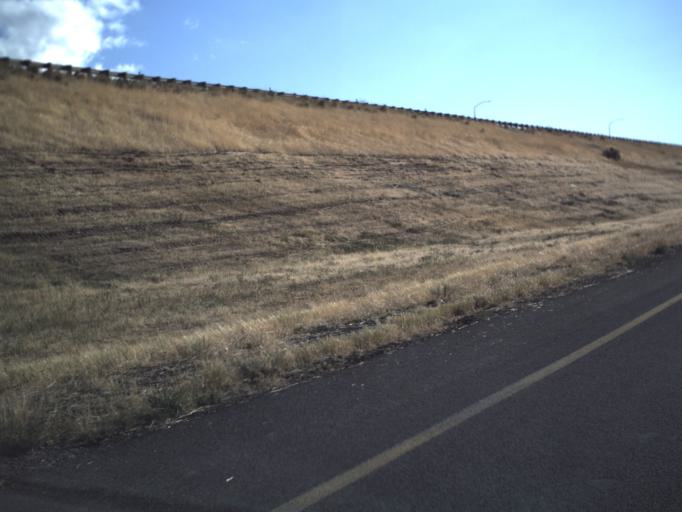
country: US
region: Utah
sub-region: Utah County
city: Santaquin
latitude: 39.9751
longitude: -111.7739
